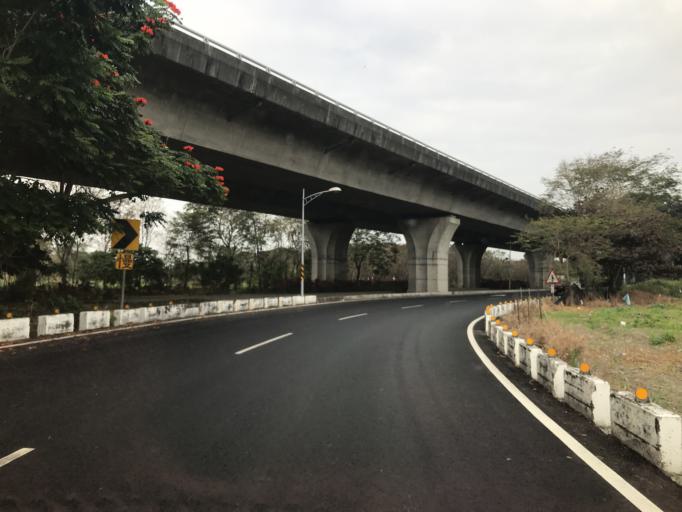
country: TW
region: Taiwan
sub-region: Pingtung
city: Pingtung
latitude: 22.6394
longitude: 120.5387
